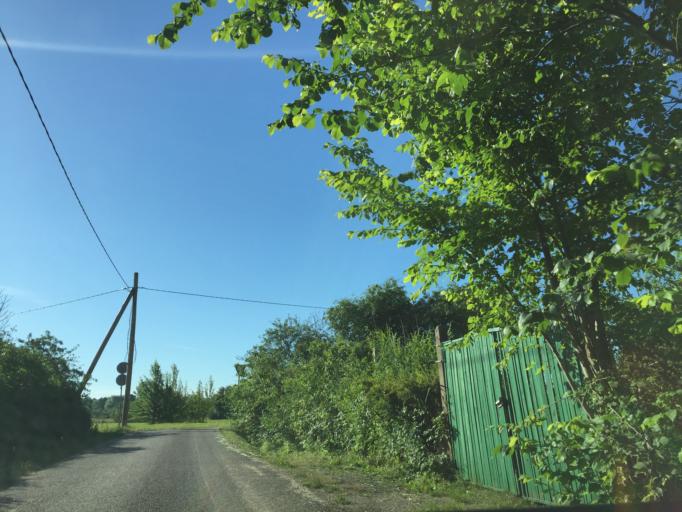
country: LV
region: Ventspils
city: Ventspils
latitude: 57.3693
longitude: 21.6085
